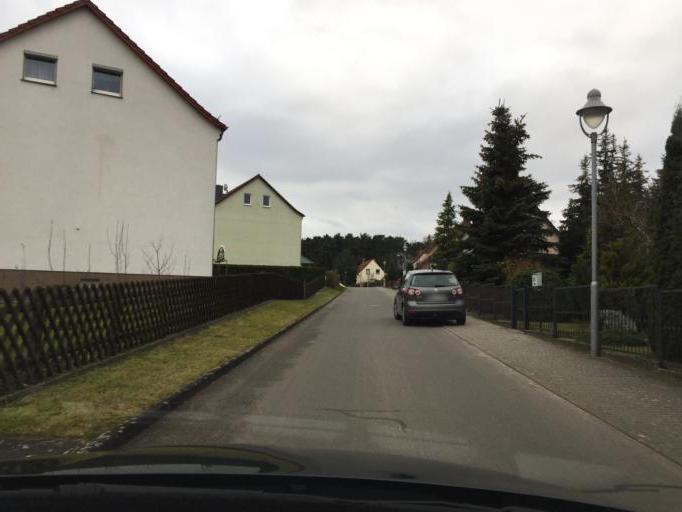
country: DE
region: Brandenburg
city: Ziltendorf
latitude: 52.2025
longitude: 14.6252
